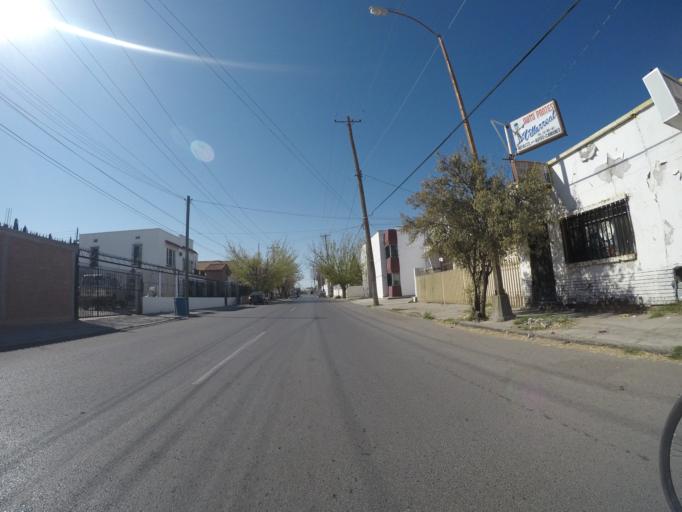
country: MX
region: Chihuahua
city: Ciudad Juarez
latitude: 31.7404
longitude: -106.4738
